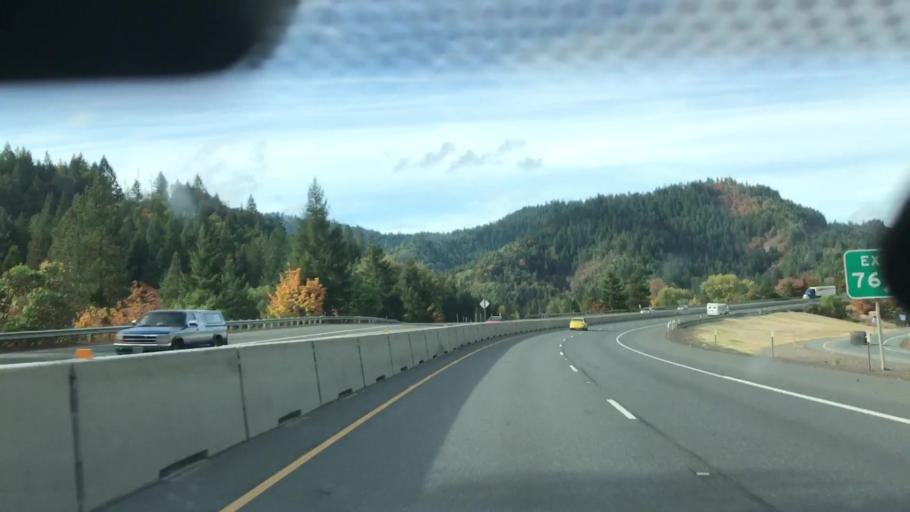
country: US
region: Oregon
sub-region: Josephine County
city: Merlin
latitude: 42.6880
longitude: -123.3924
